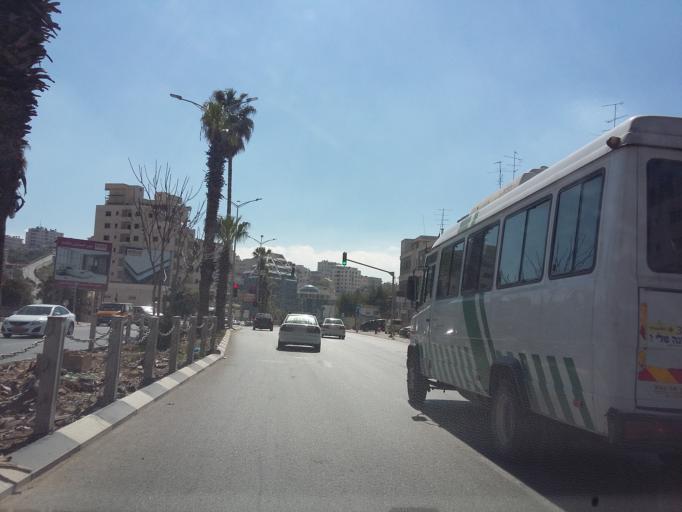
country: PS
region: West Bank
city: Ramallah
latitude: 31.8879
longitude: 35.2174
